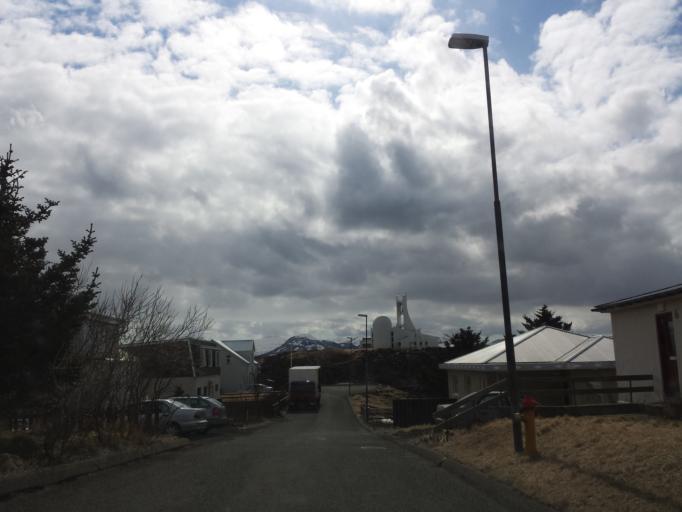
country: IS
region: West
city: Stykkisholmur
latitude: 65.0765
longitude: -22.7208
